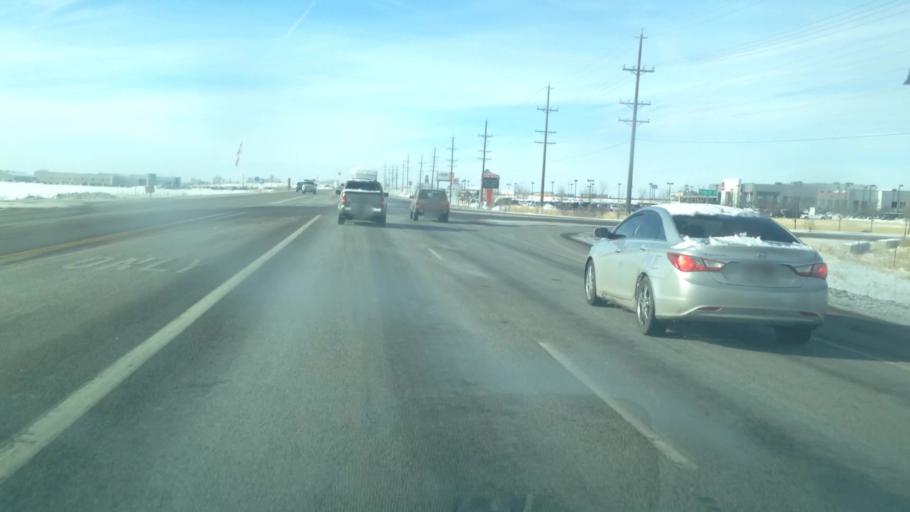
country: US
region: Idaho
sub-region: Bonneville County
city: Idaho Falls
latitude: 43.4678
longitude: -112.0724
